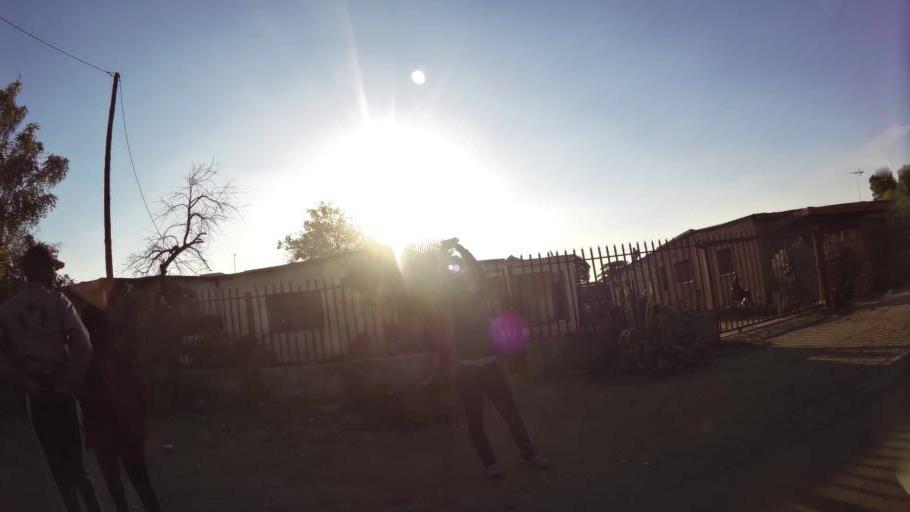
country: ZA
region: North-West
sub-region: Bojanala Platinum District Municipality
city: Rustenburg
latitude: -25.6398
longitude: 27.2175
